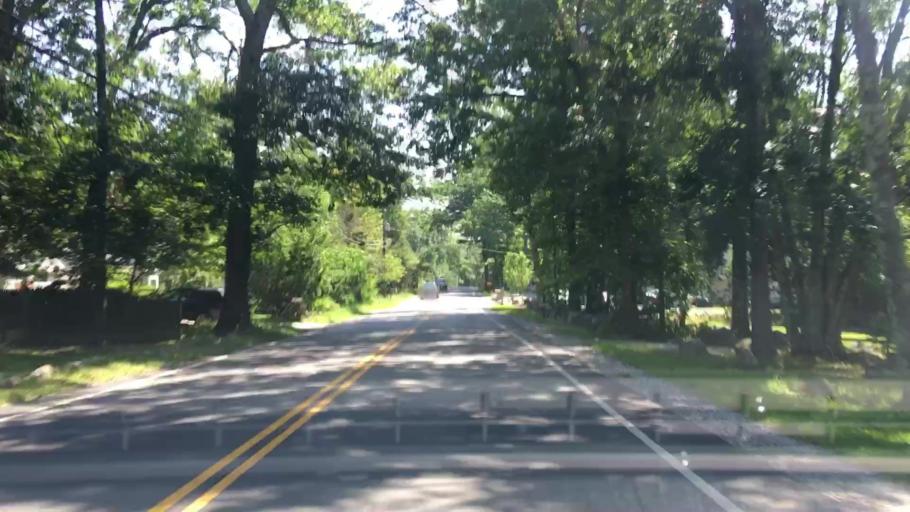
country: US
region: New Hampshire
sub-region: Rockingham County
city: Hampstead
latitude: 42.8570
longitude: -71.2203
